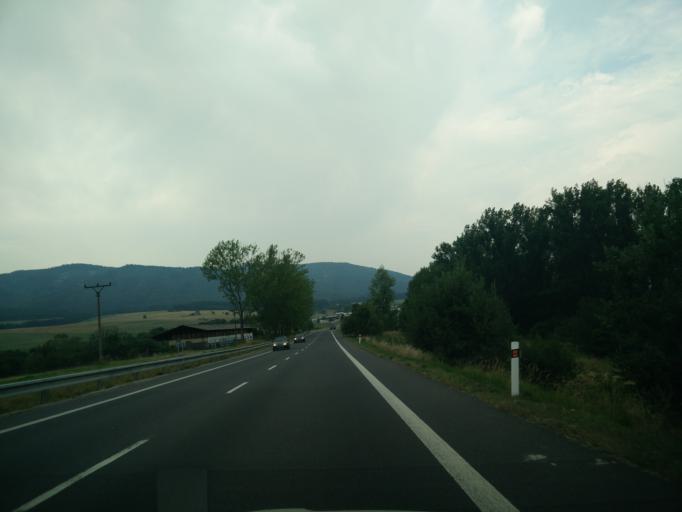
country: SK
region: Banskobystricky
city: Ziar nad Hronom
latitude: 48.6256
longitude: 18.7885
